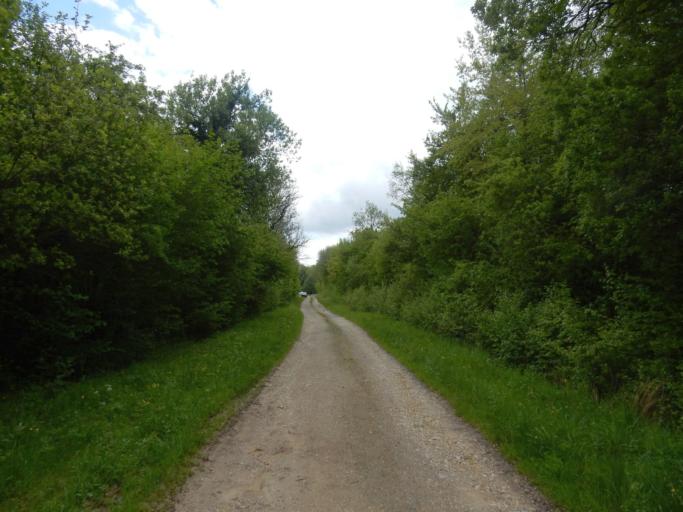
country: FR
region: Lorraine
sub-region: Departement de la Meuse
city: Verdun
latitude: 49.1980
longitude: 5.4339
